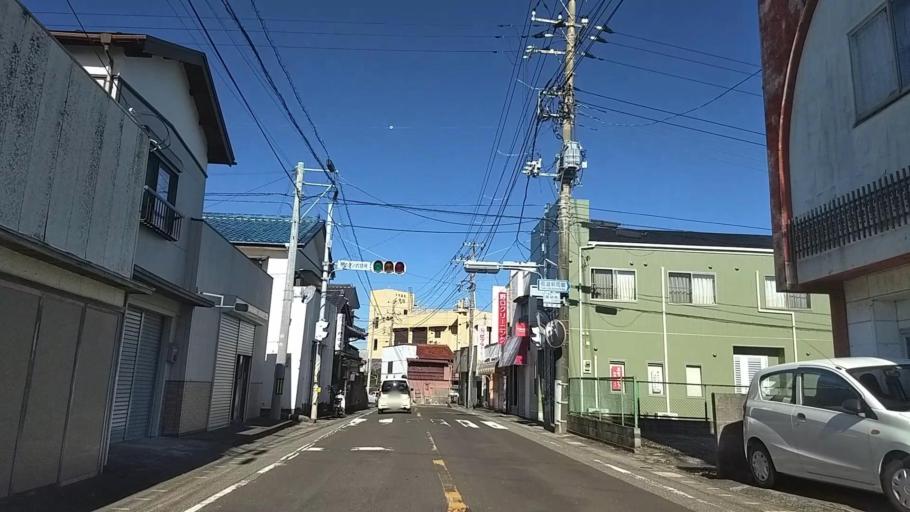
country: JP
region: Chiba
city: Tateyama
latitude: 34.9620
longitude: 139.9583
